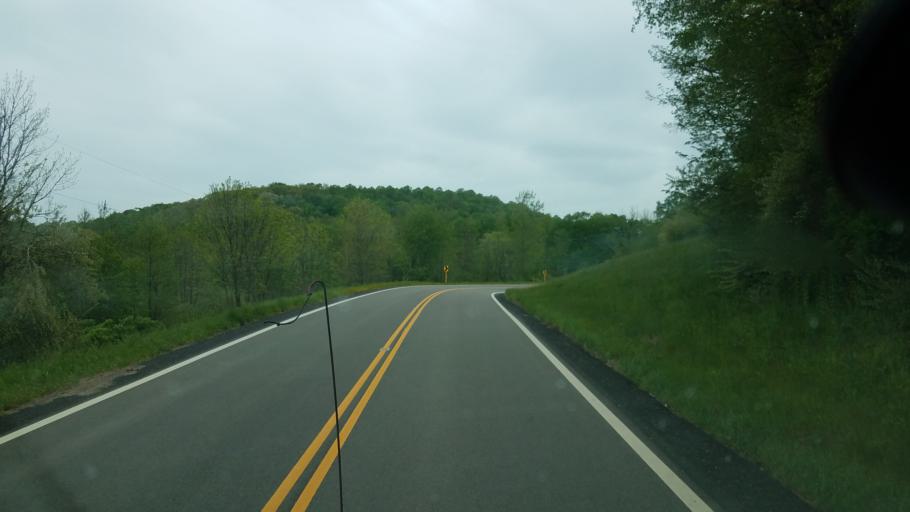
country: US
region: Ohio
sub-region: Coshocton County
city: West Lafayette
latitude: 40.2198
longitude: -81.7900
